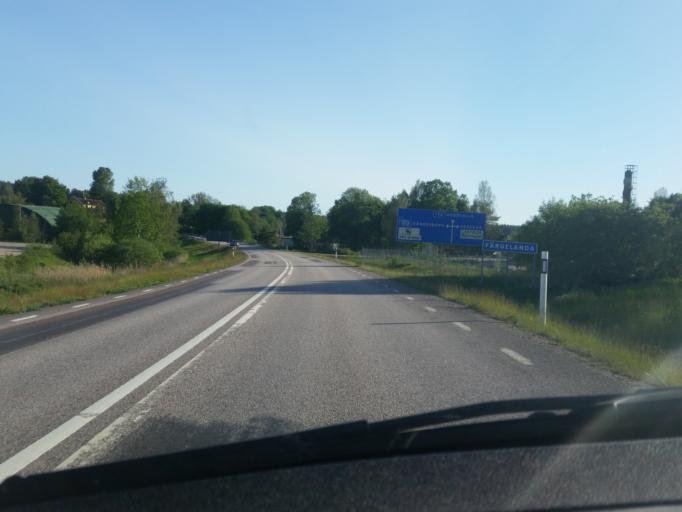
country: SE
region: Vaestra Goetaland
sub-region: Fargelanda Kommun
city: Faergelanda
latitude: 58.5750
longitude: 12.0072
